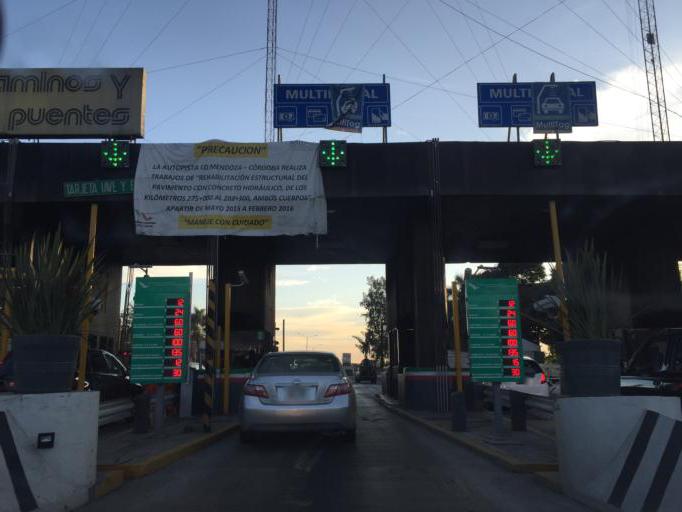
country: MX
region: Veracruz
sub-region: Fortin
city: Fortin de las Flores
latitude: 18.9070
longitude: -96.9997
